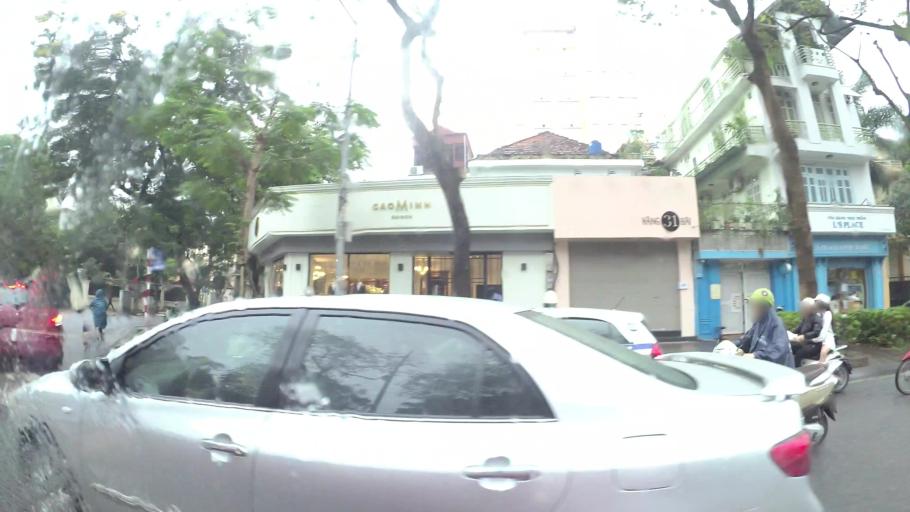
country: VN
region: Ha Noi
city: Hanoi
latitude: 21.0244
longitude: 105.8467
